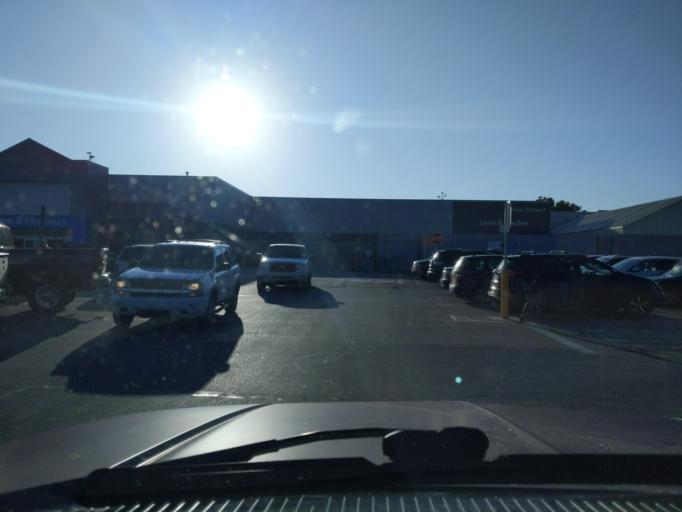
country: US
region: Oklahoma
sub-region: Tulsa County
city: Sand Springs
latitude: 36.1355
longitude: -96.1192
